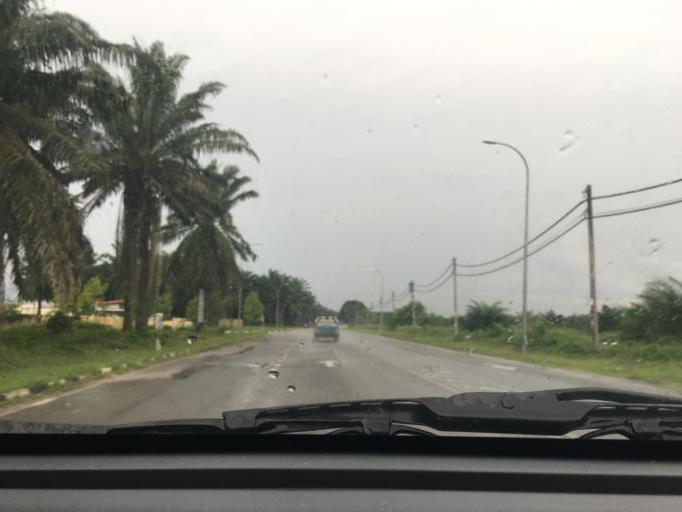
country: MY
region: Kedah
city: Sungai Petani
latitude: 5.5909
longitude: 100.6394
